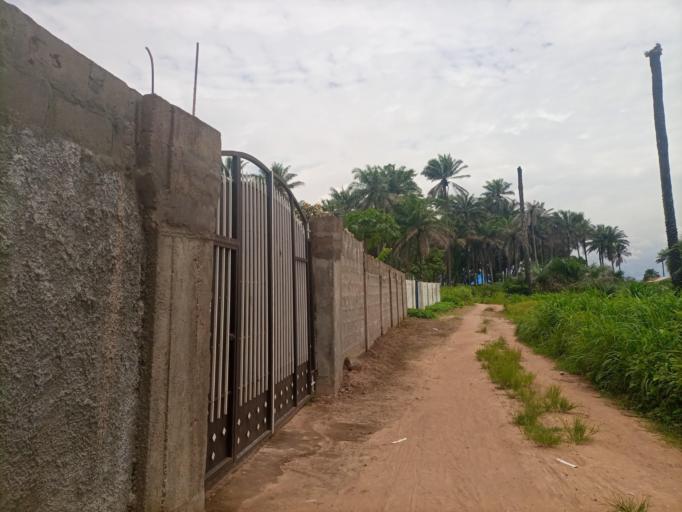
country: SL
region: Northern Province
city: Masoyila
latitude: 8.5555
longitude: -13.1665
